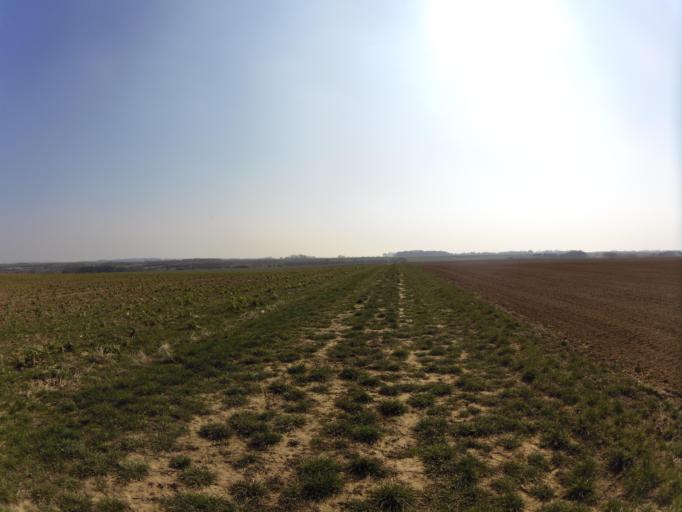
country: DE
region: Bavaria
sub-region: Regierungsbezirk Unterfranken
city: Giebelstadt
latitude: 49.6778
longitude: 9.9800
